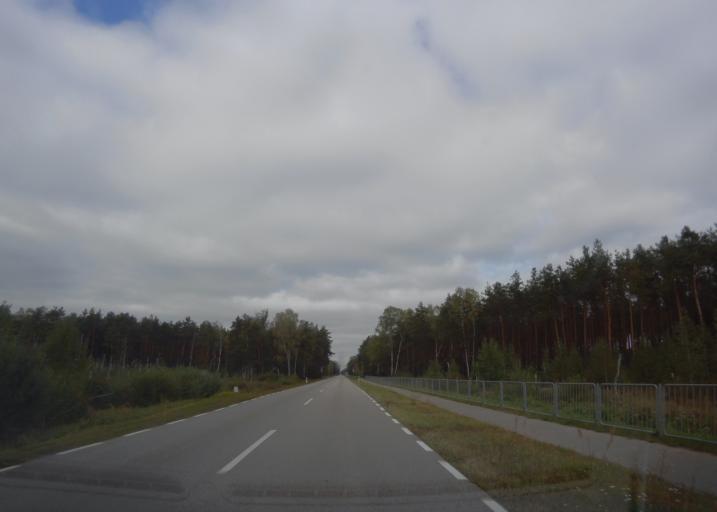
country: PL
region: Lublin Voivodeship
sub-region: Powiat wlodawski
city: Wlodawa
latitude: 51.4855
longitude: 23.5166
